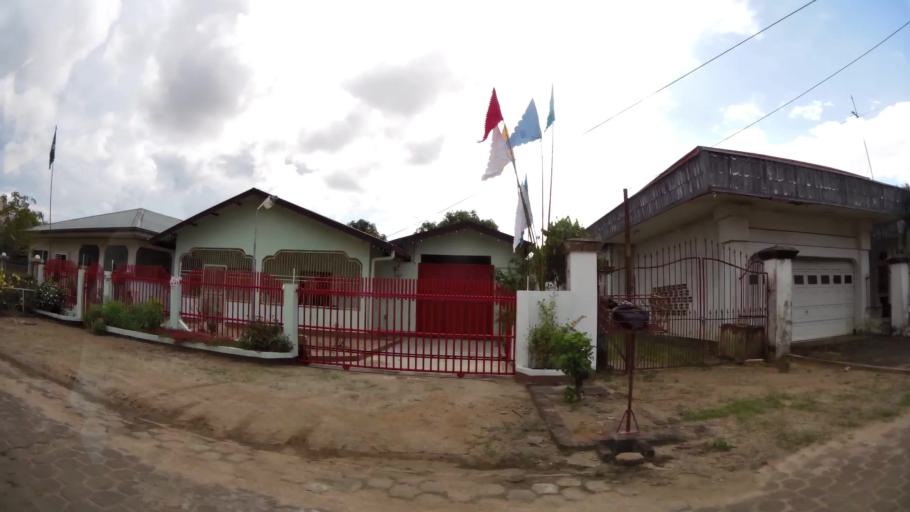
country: SR
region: Paramaribo
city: Paramaribo
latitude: 5.8574
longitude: -55.1775
